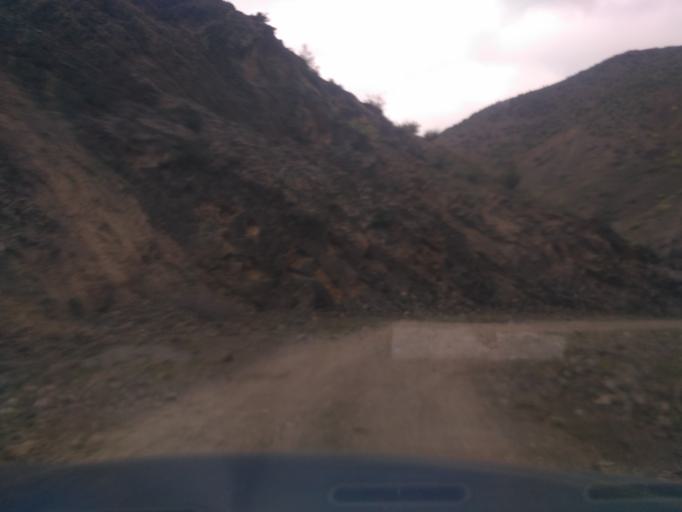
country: UZ
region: Jizzax
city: Zomin
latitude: 39.8594
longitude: 68.3848
